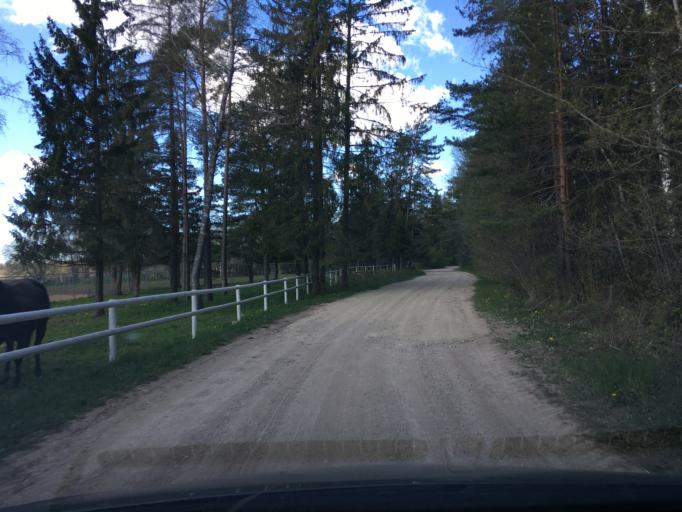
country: EE
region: Harju
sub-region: Raasiku vald
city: Raasiku
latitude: 59.2117
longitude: 25.1709
